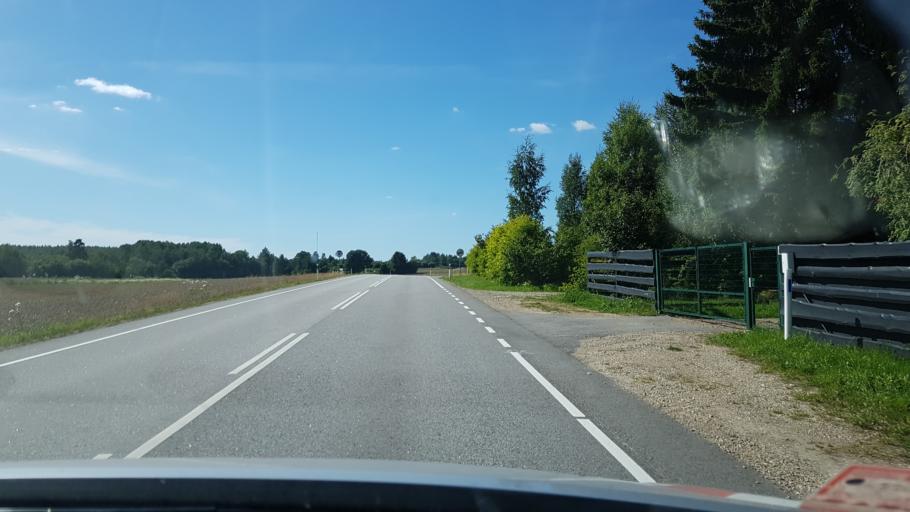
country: EE
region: Polvamaa
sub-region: Polva linn
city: Polva
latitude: 58.0597
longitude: 26.9181
